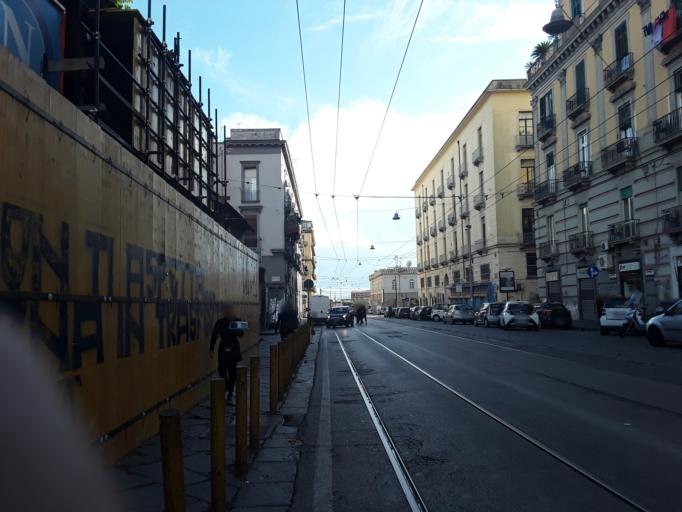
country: IT
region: Campania
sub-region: Provincia di Napoli
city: Napoli
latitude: 40.8484
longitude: 14.2688
